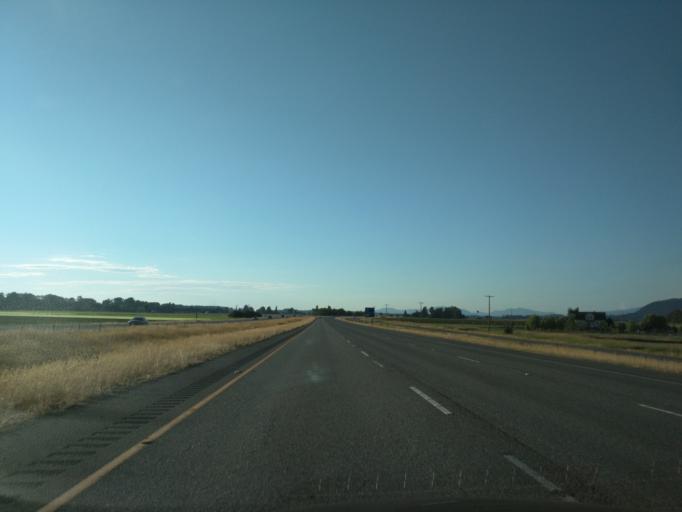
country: US
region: Washington
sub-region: Snohomish County
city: Stanwood
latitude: 48.3248
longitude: -122.3296
